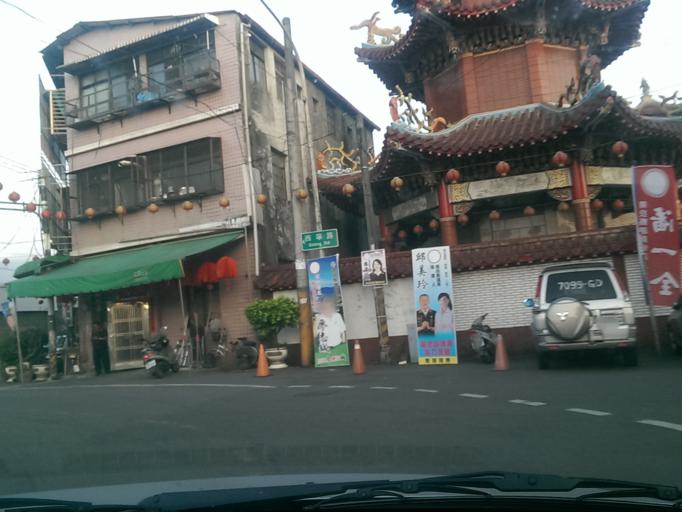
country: TW
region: Taiwan
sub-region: Nantou
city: Puli
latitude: 23.9657
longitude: 120.9621
